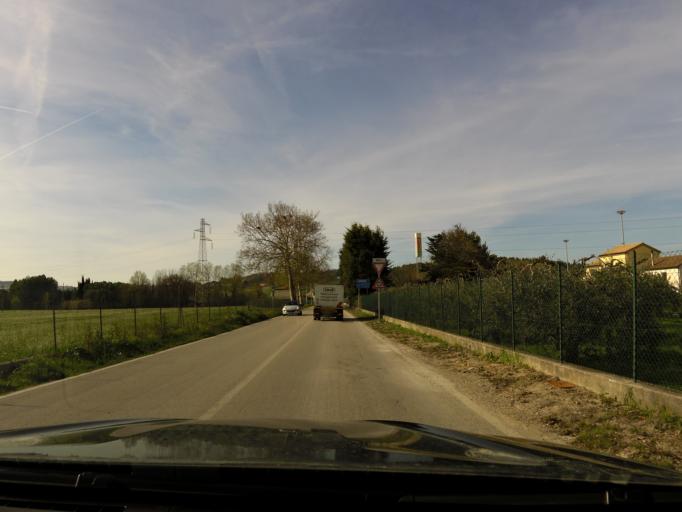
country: IT
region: The Marches
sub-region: Provincia di Ancona
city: Villa Musone
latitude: 43.4533
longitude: 13.5977
